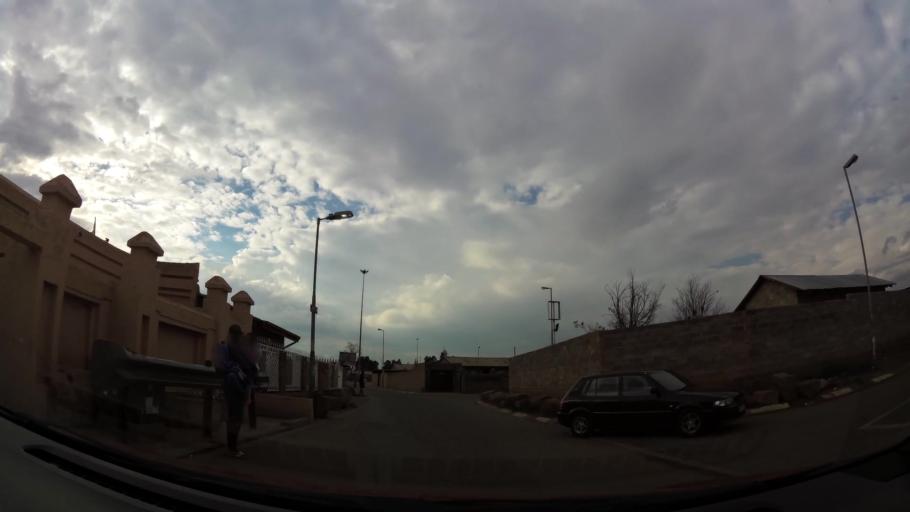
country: ZA
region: Gauteng
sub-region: City of Johannesburg Metropolitan Municipality
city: Soweto
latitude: -26.2504
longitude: 27.8242
